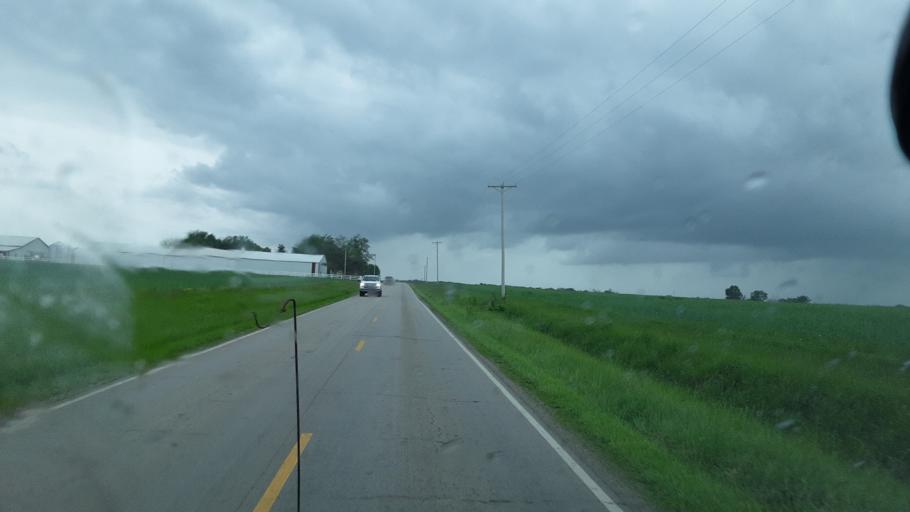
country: US
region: Missouri
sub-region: Monroe County
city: Paris
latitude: 39.4658
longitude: -92.2127
